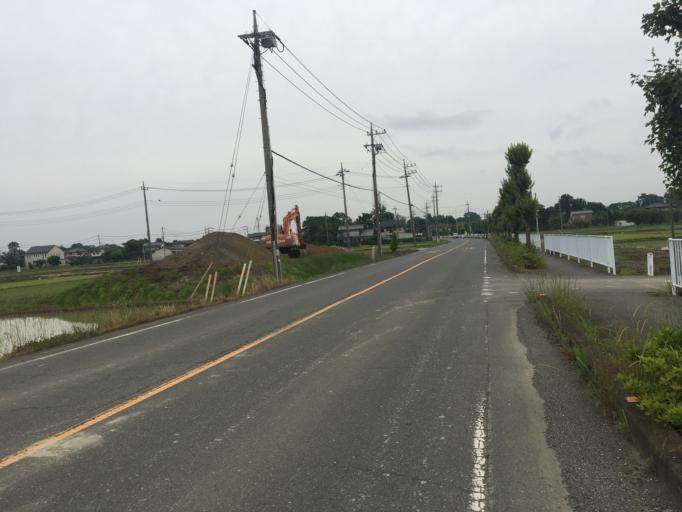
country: JP
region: Saitama
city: Sakado
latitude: 35.9981
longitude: 139.4389
